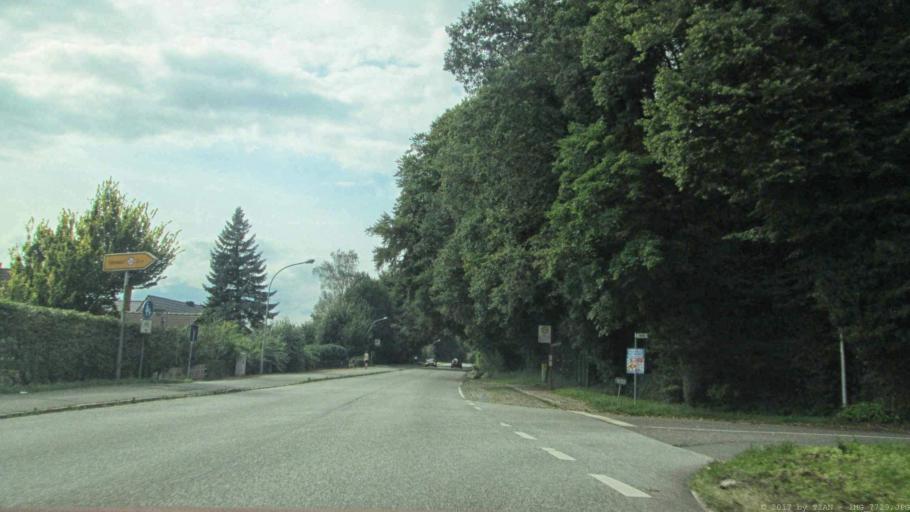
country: DE
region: Schleswig-Holstein
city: Escheburg
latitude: 53.4606
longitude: 10.3279
